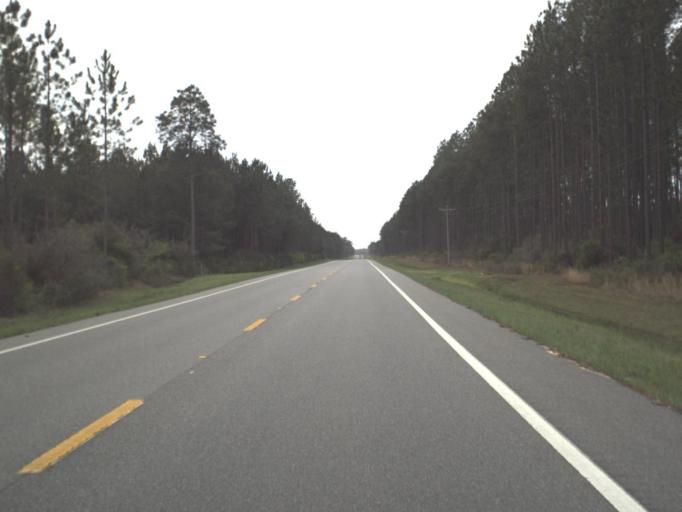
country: US
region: Florida
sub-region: Gulf County
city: Wewahitchka
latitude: 30.3115
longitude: -85.2329
